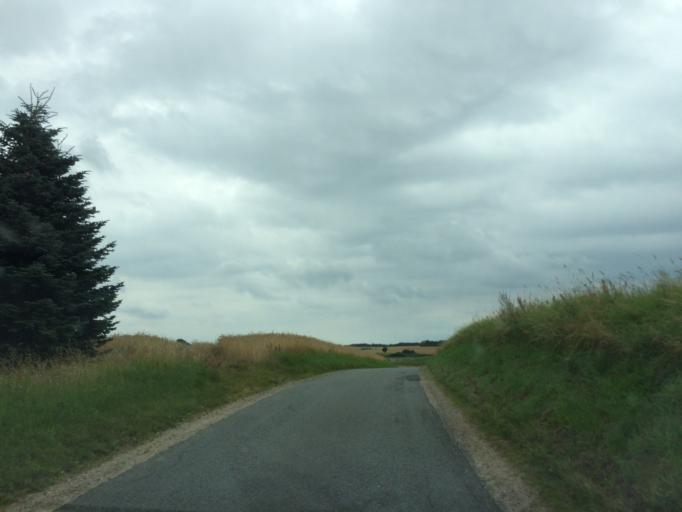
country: DK
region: Central Jutland
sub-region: Syddjurs Kommune
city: Ronde
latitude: 56.2405
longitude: 10.5356
